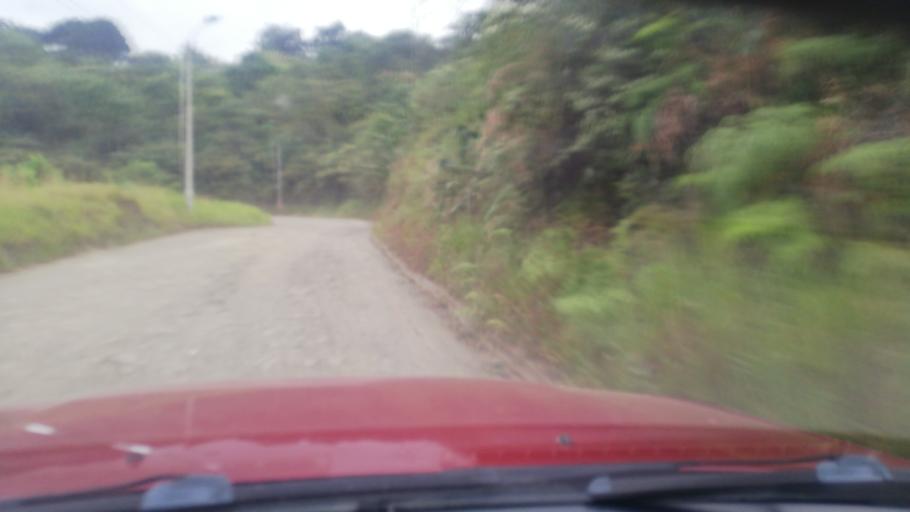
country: CO
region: Valle del Cauca
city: Cali
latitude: 3.4922
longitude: -76.5468
